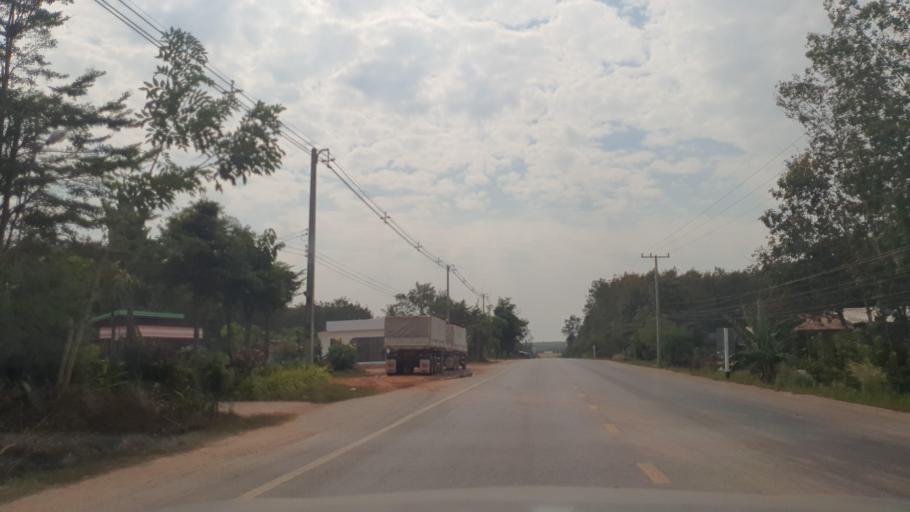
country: TH
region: Changwat Bueng Kan
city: Si Wilai
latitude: 18.2968
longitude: 103.8015
